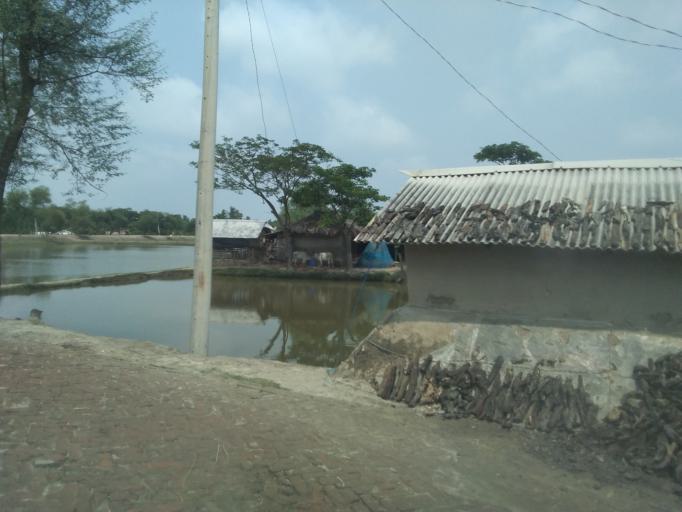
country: BD
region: Khulna
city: Phultala
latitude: 22.6416
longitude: 89.4261
